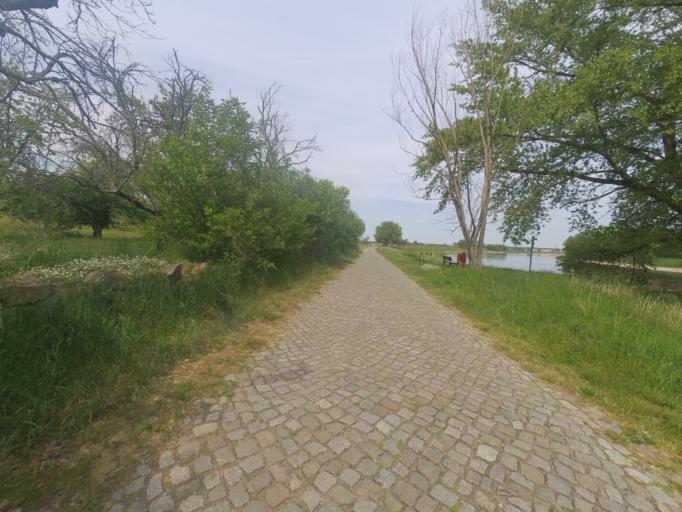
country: DE
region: Saxony
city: Strehla
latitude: 51.3651
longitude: 13.2289
